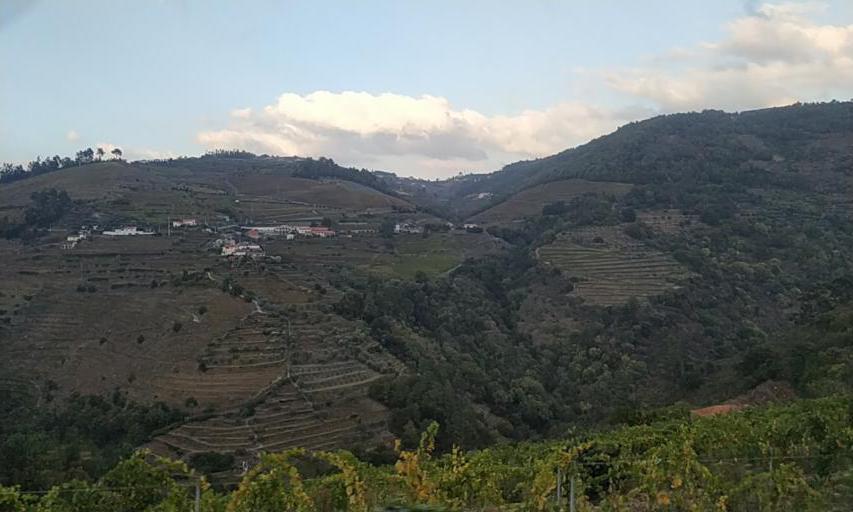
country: PT
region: Vila Real
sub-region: Mesao Frio
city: Mesao Frio
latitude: 41.1821
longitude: -7.8465
